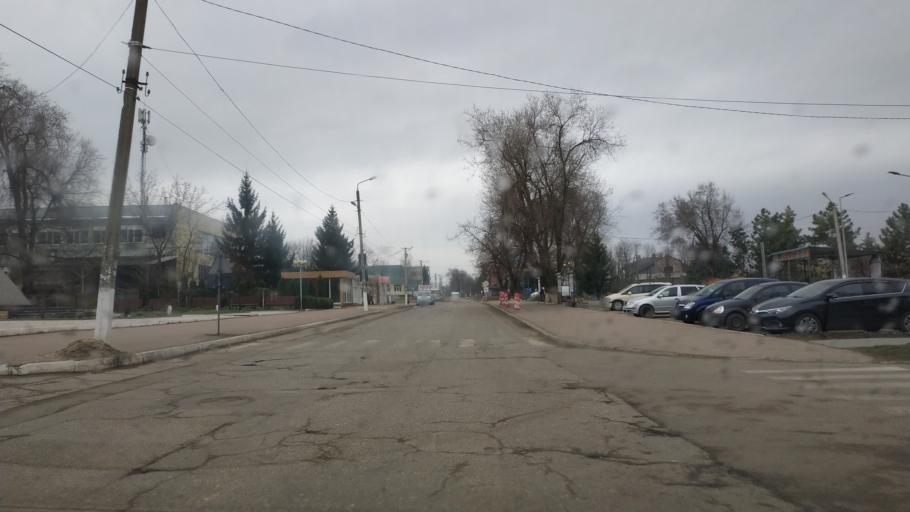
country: MD
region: Leova
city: Leova
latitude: 46.4791
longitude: 28.2533
